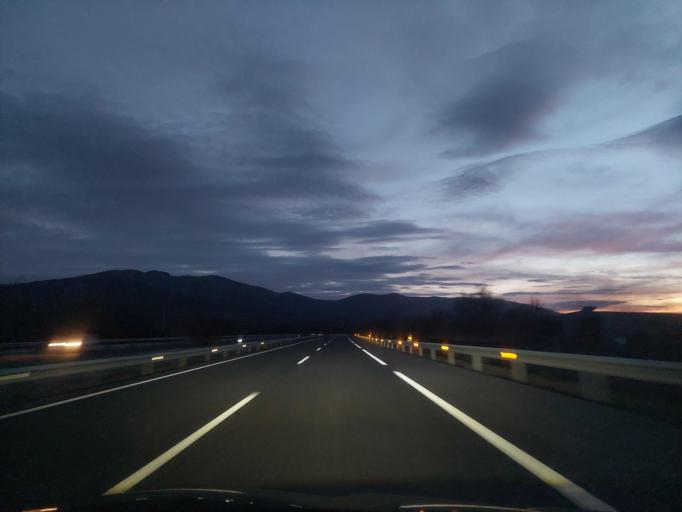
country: ES
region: Castille and Leon
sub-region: Provincia de Segovia
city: Segovia
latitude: 40.8843
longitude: -4.1172
